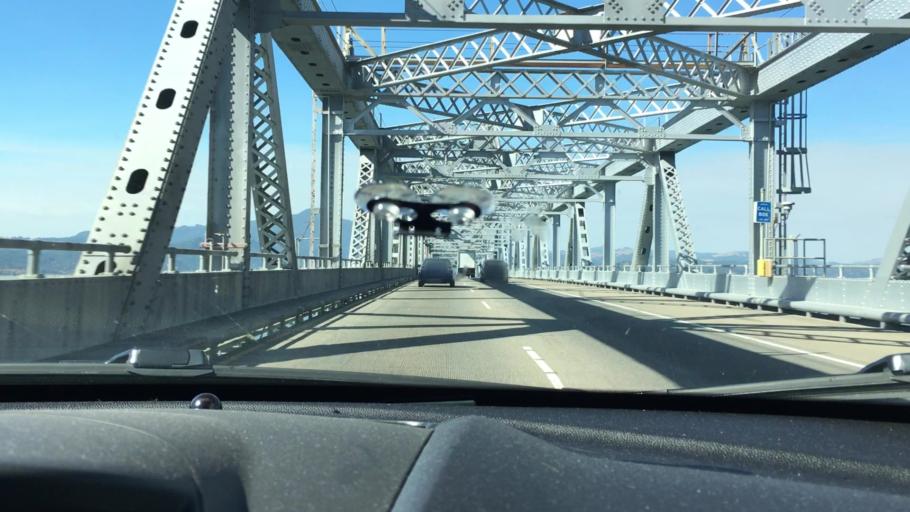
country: US
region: California
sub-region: Marin County
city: Tiburon
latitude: 37.9351
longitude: -122.4443
